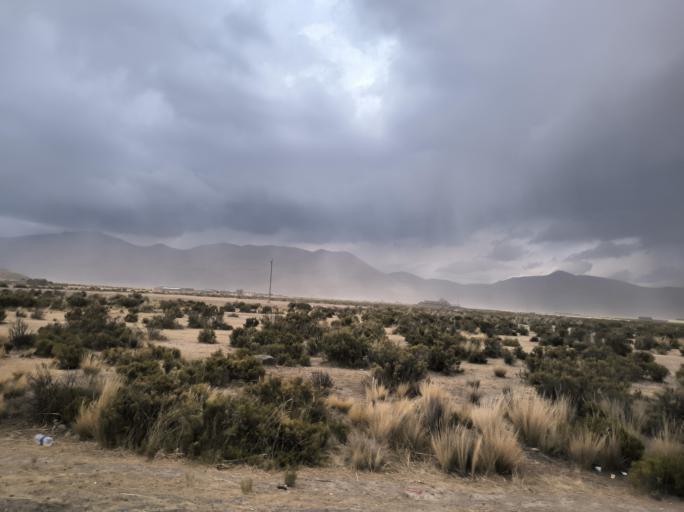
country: BO
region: Oruro
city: Challapata
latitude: -18.7735
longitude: -66.8546
